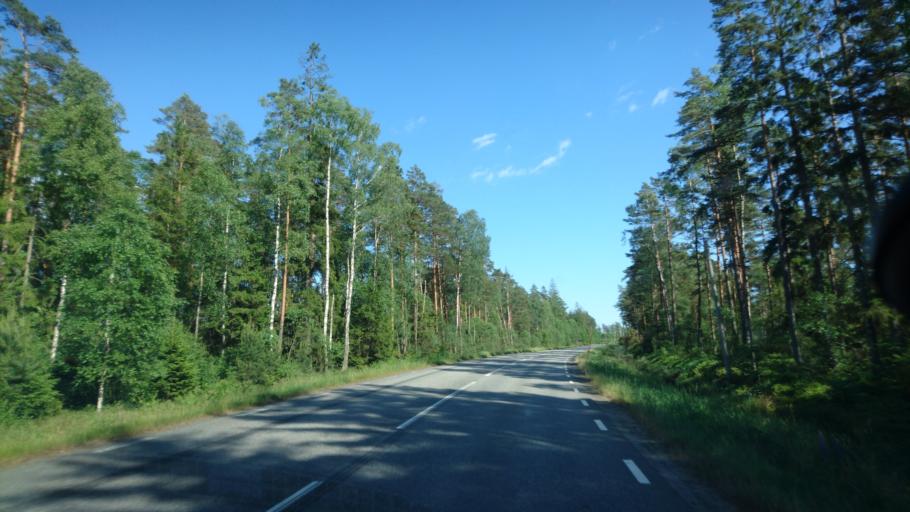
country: SE
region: Skane
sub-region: Osby Kommun
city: Lonsboda
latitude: 56.4306
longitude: 14.2663
